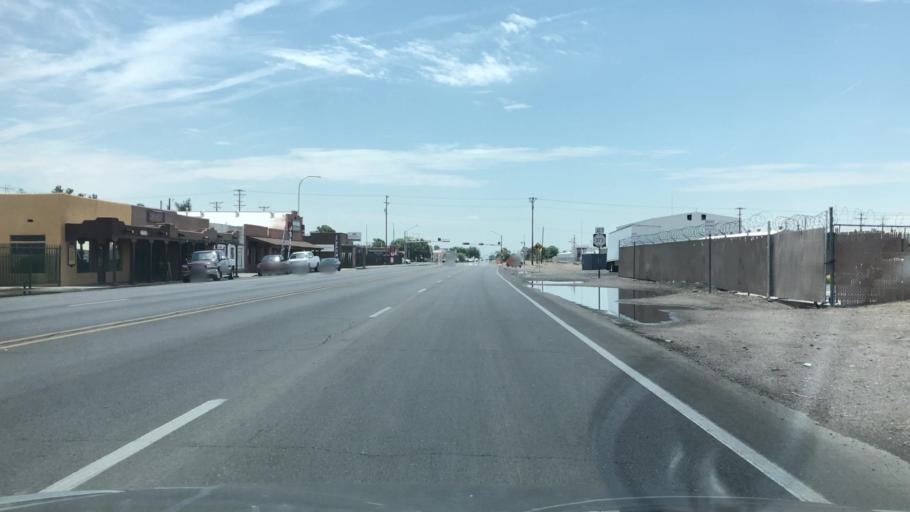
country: US
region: New Mexico
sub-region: Dona Ana County
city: University Park
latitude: 32.2766
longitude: -106.7674
